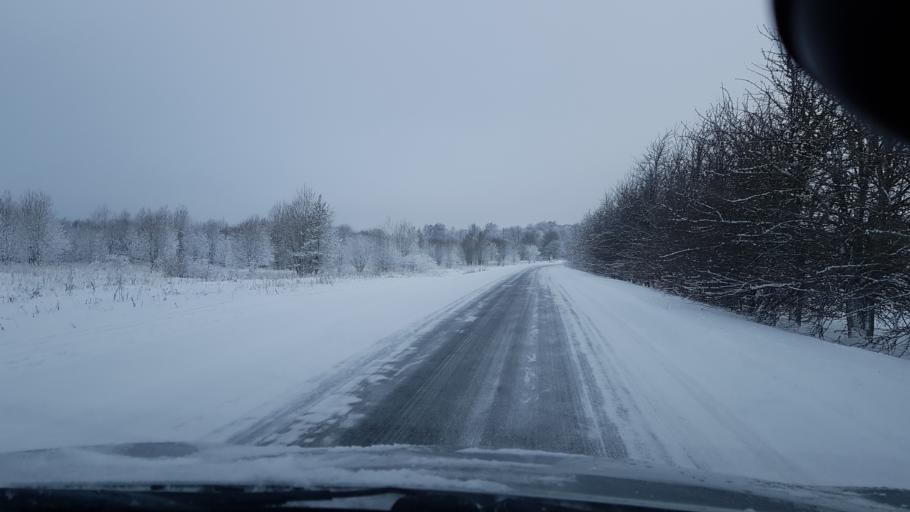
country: EE
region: Harju
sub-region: Keila linn
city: Keila
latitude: 59.3354
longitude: 24.3967
